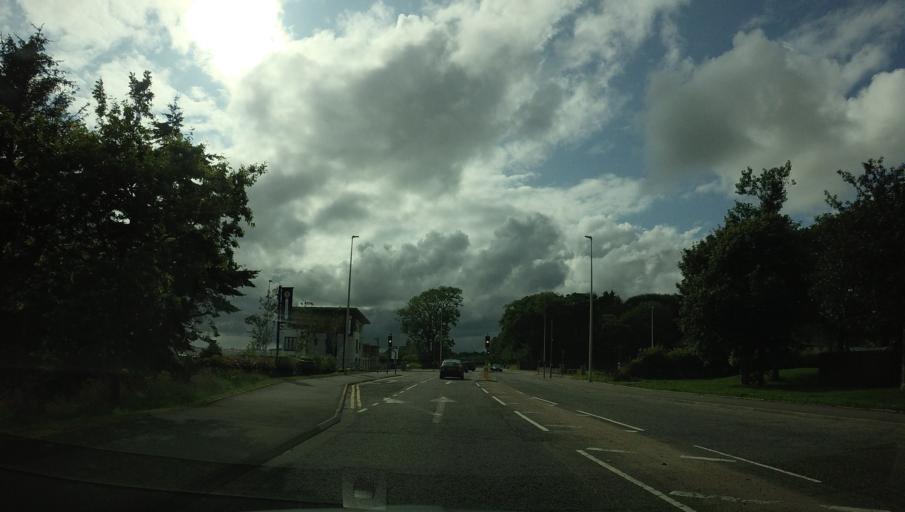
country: GB
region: Scotland
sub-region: Aberdeen City
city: Cults
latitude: 57.1505
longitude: -2.1818
